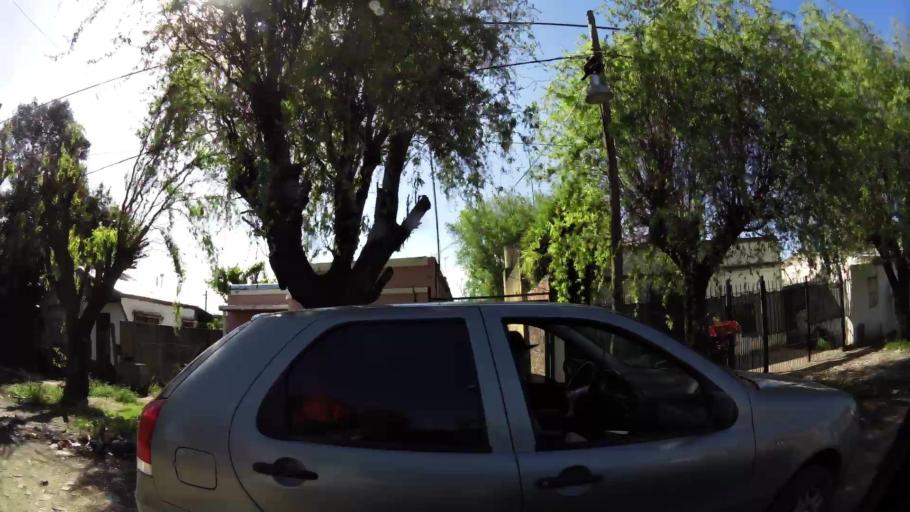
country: AR
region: Buenos Aires
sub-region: Partido de Quilmes
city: Quilmes
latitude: -34.8029
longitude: -58.2553
